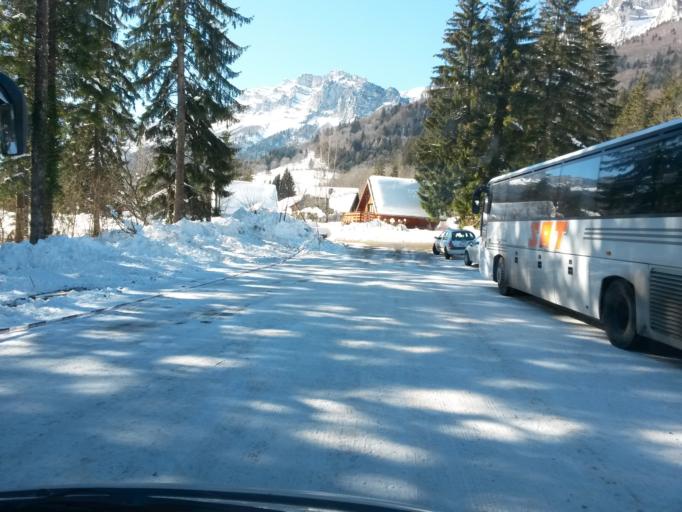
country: FR
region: Rhone-Alpes
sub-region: Departement de l'Isere
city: Le Touvet
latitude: 45.3547
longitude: 5.9189
